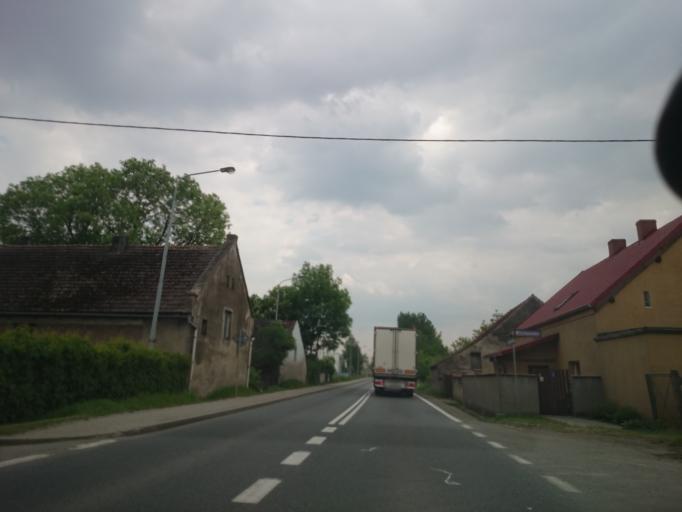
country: PL
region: Lower Silesian Voivodeship
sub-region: Powiat wroclawski
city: Kobierzyce
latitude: 50.9399
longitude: 16.9001
